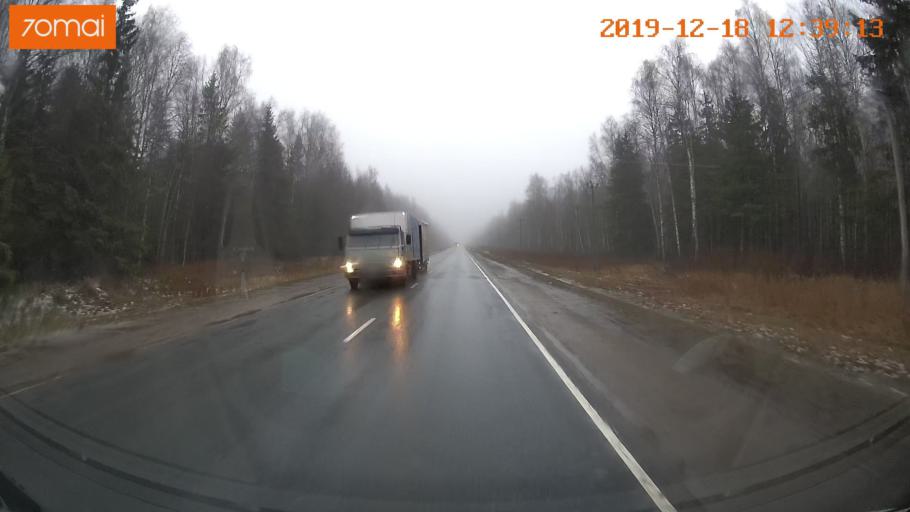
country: RU
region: Moskovskaya
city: Vysokovsk
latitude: 56.1621
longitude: 36.6100
